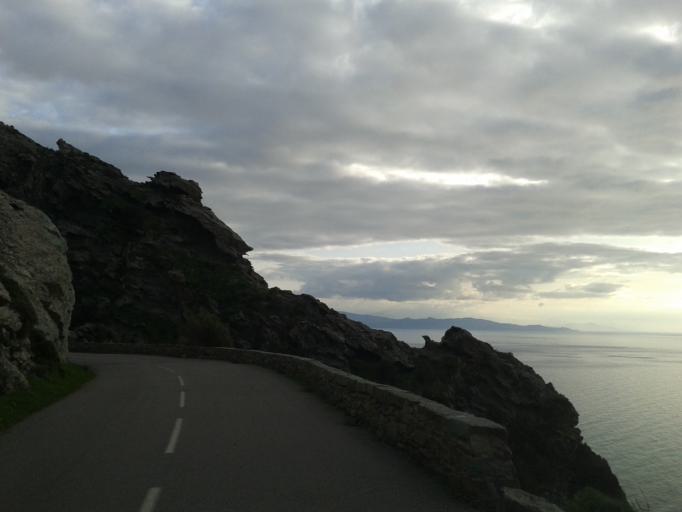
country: FR
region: Corsica
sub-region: Departement de la Haute-Corse
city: Brando
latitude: 42.8779
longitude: 9.3304
